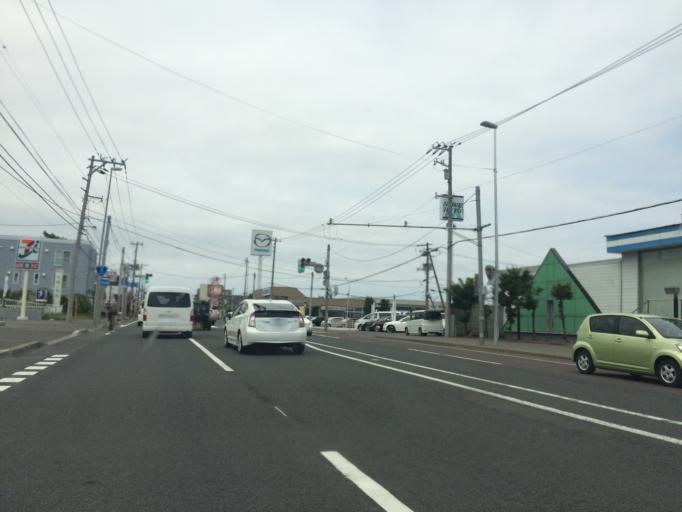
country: JP
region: Hokkaido
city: Sapporo
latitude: 43.1026
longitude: 141.2523
